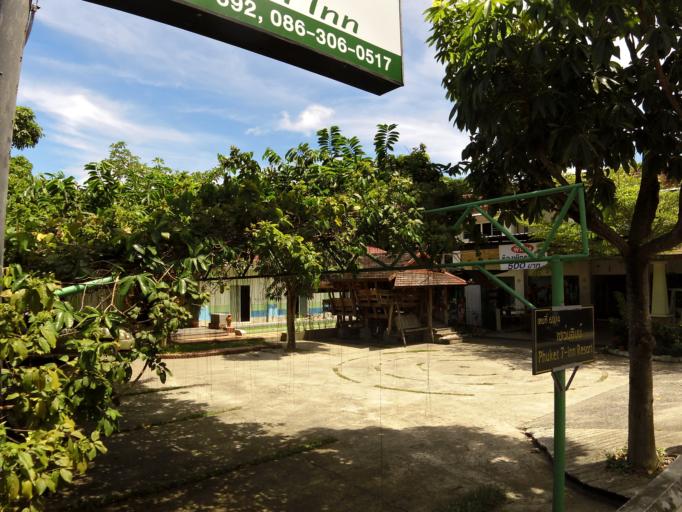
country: TH
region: Phuket
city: Ban Chalong
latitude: 7.8260
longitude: 98.3378
